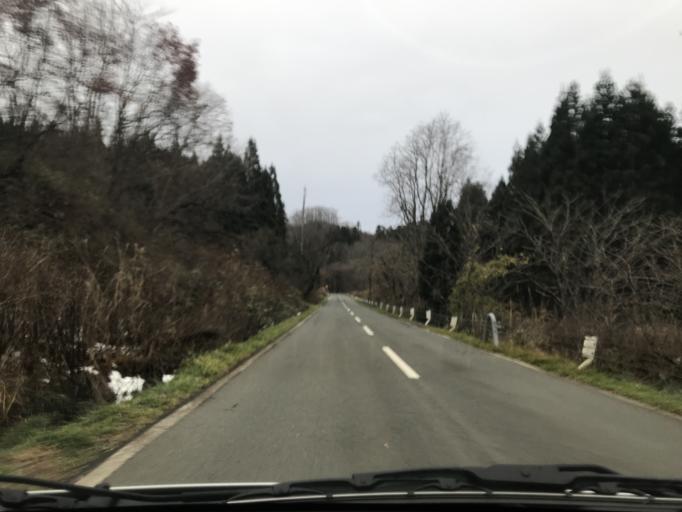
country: JP
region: Iwate
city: Tono
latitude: 39.1610
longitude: 141.3652
